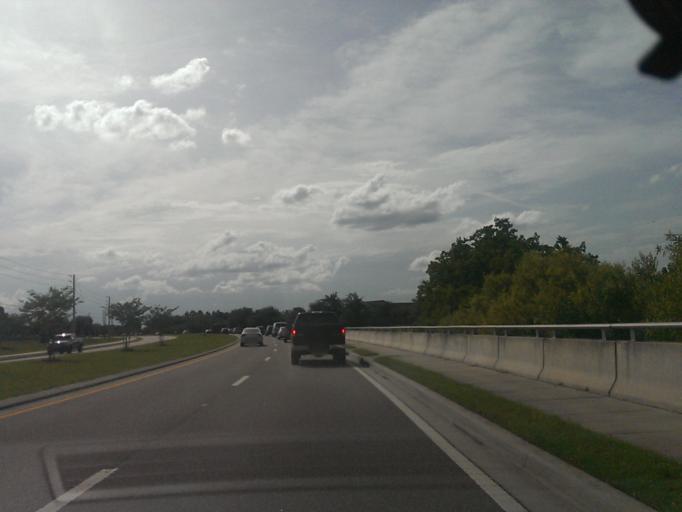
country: US
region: Florida
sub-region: Orange County
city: Lake Butler
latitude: 28.4775
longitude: -81.5732
